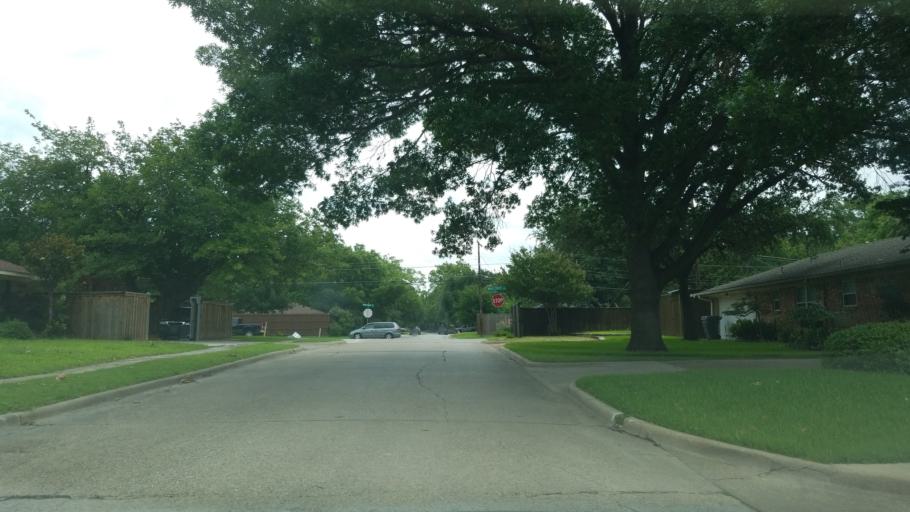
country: US
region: Texas
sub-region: Dallas County
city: Farmers Branch
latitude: 32.8895
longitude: -96.8711
